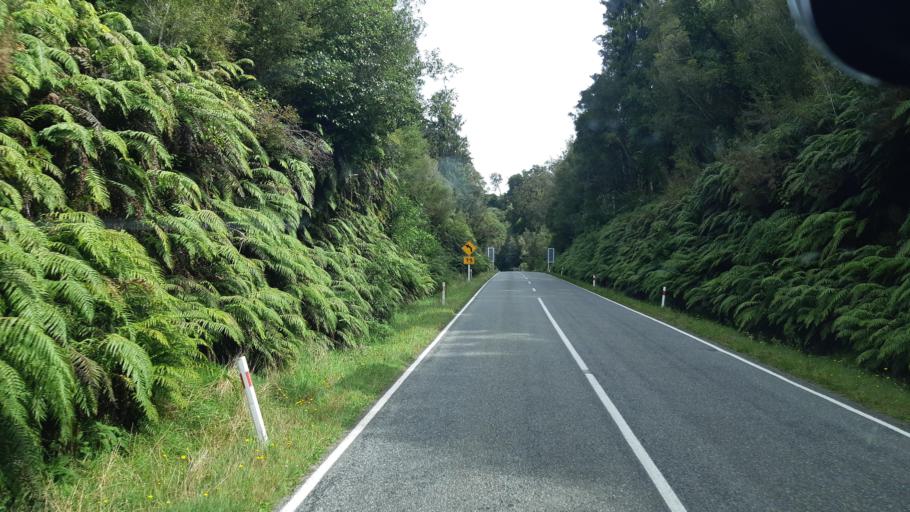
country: NZ
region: West Coast
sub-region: Westland District
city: Hokitika
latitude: -42.9813
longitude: 170.6833
